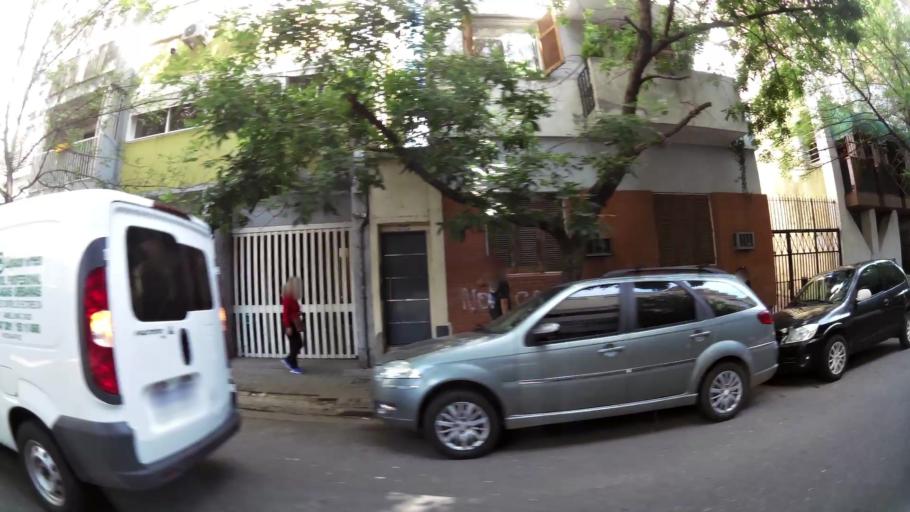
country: AR
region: Santa Fe
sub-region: Departamento de Rosario
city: Rosario
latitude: -32.9535
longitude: -60.6297
